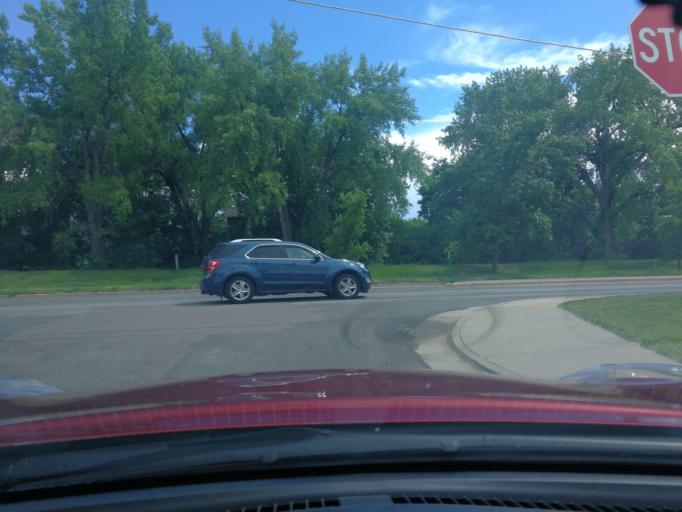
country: US
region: Colorado
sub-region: Arapahoe County
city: Littleton
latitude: 39.5903
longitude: -104.9908
